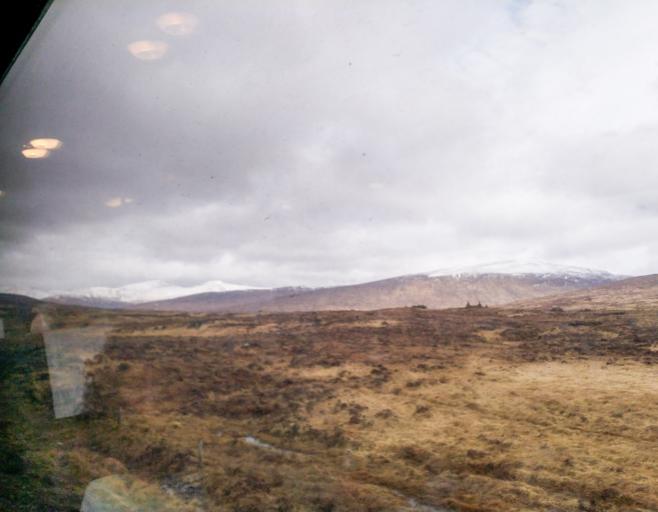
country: GB
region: Scotland
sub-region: Highland
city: Spean Bridge
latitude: 56.7384
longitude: -4.6606
